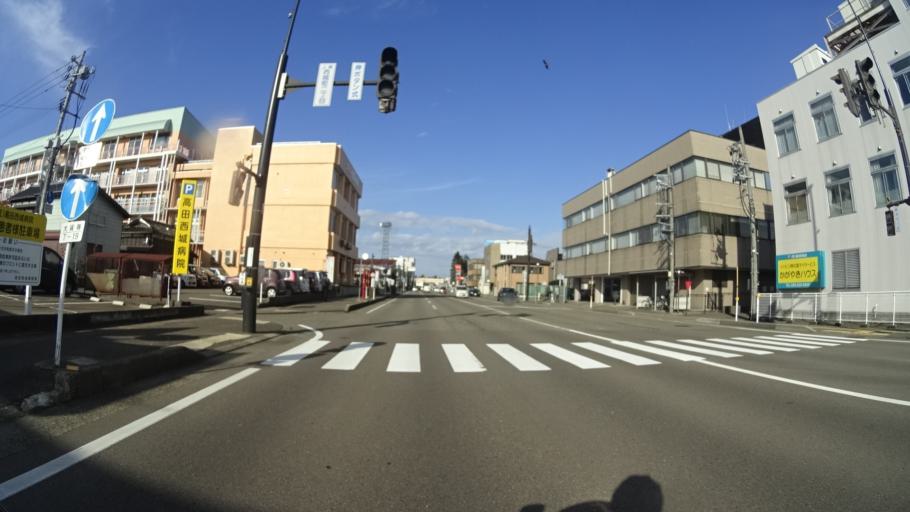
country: JP
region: Niigata
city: Joetsu
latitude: 37.1110
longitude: 138.2505
